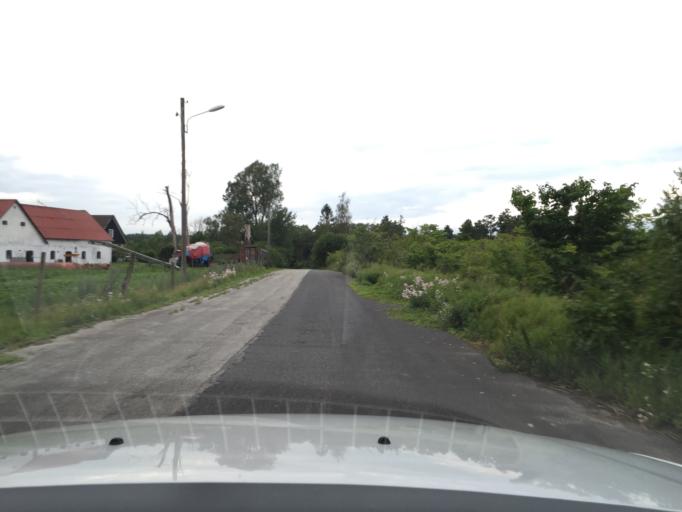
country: SE
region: Skane
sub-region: Kristianstads Kommun
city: Norra Asum
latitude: 55.9362
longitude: 14.0756
